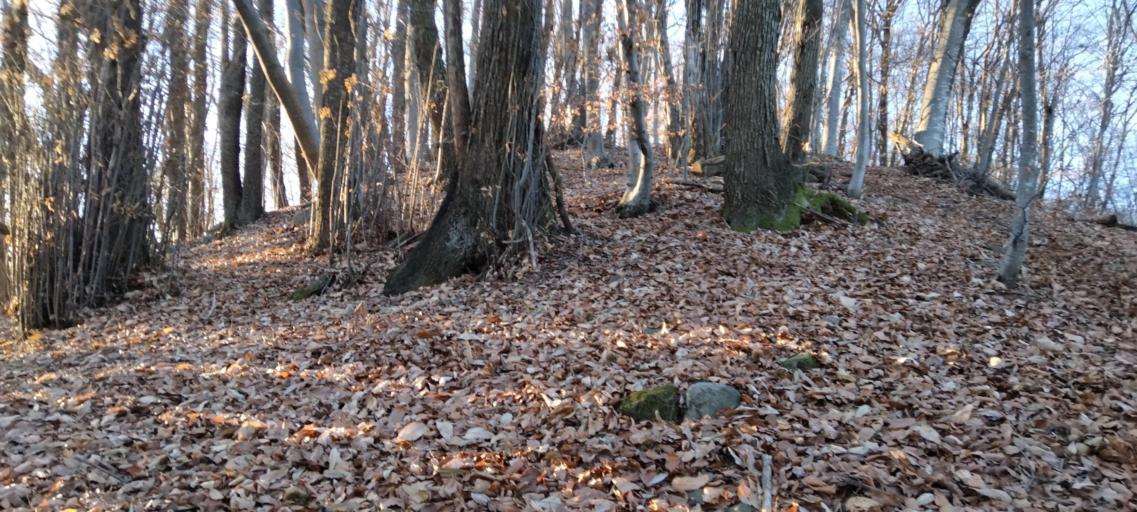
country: IT
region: Veneto
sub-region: Provincia di Vicenza
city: Valdagno
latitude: 45.6723
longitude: 11.3242
